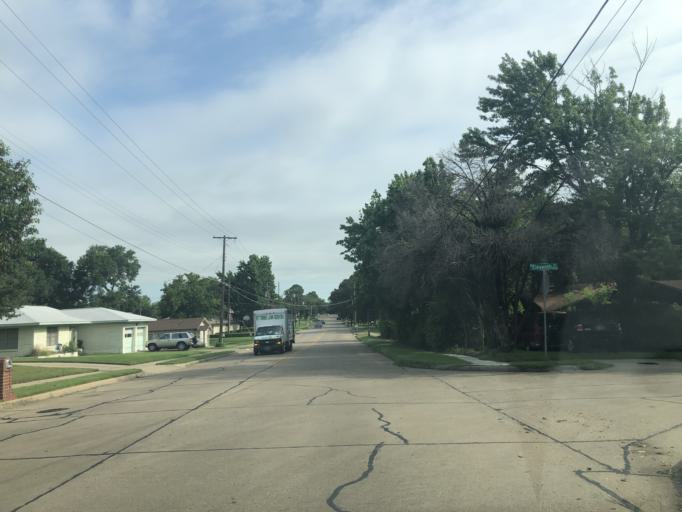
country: US
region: Texas
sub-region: Dallas County
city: Irving
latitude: 32.8048
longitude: -96.9708
